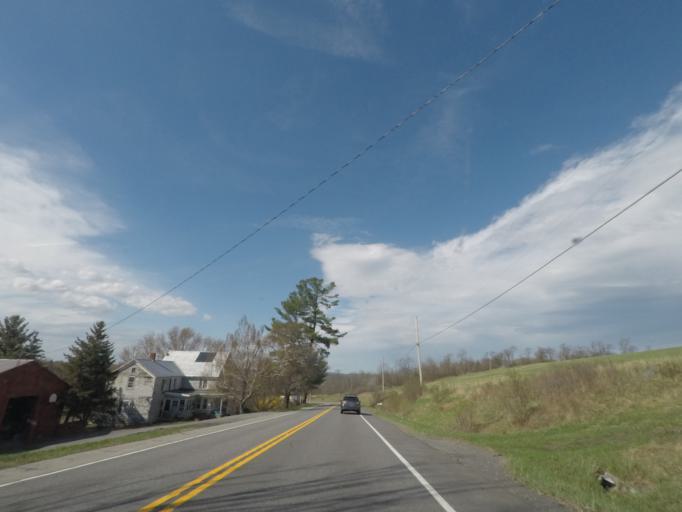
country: US
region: New York
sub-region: Greene County
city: Cairo
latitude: 42.4707
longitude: -74.0006
